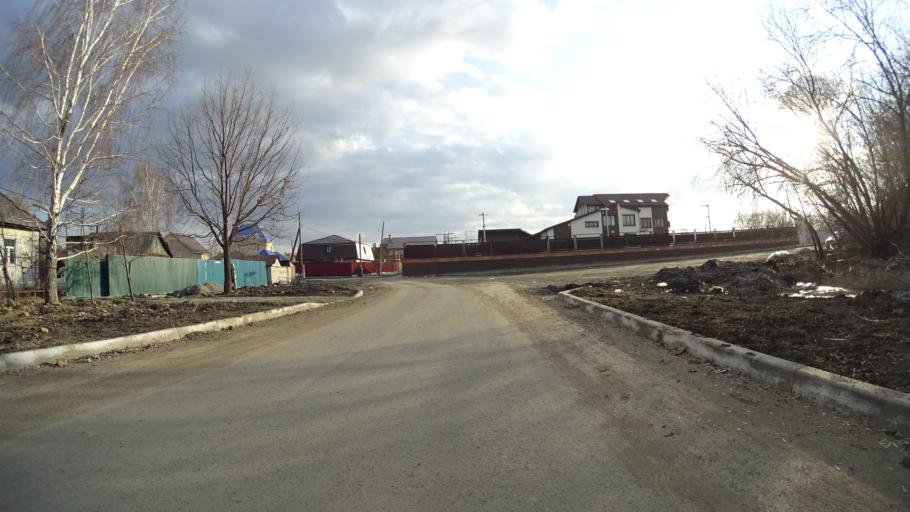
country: RU
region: Chelyabinsk
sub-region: Gorod Chelyabinsk
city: Chelyabinsk
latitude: 55.1332
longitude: 61.3877
